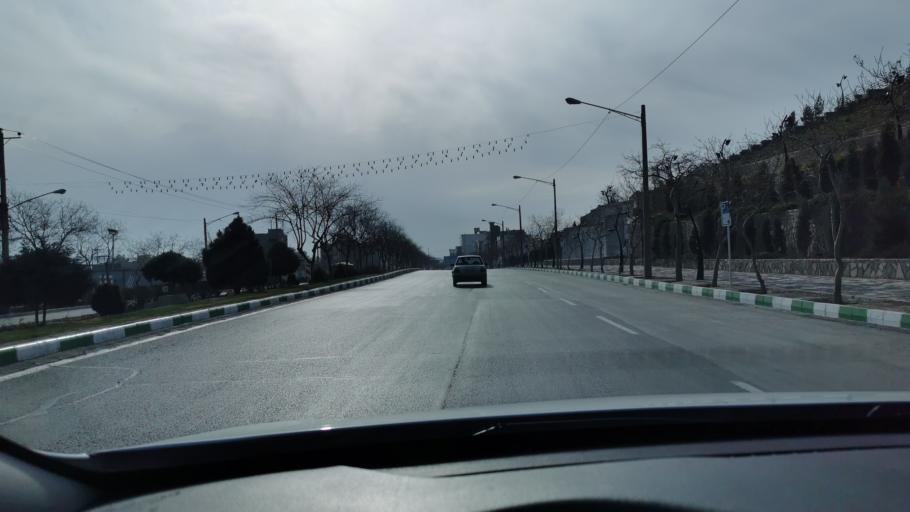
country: IR
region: Razavi Khorasan
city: Mashhad
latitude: 36.2950
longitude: 59.5308
